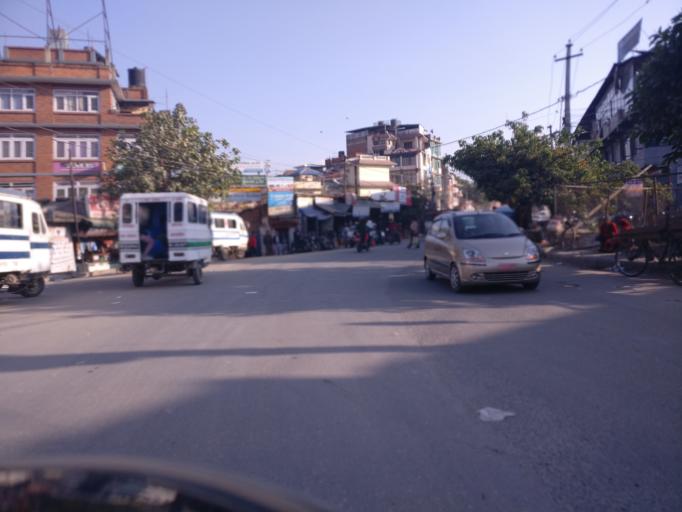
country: NP
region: Central Region
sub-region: Bagmati Zone
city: Patan
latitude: 27.6668
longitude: 85.3234
